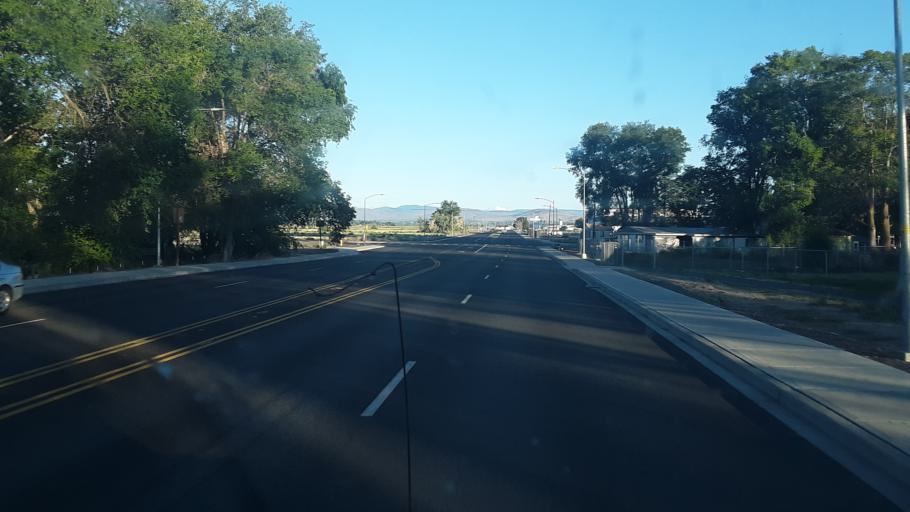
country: US
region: Washington
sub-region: Yakima County
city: Yakima
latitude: 46.5646
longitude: -120.5183
